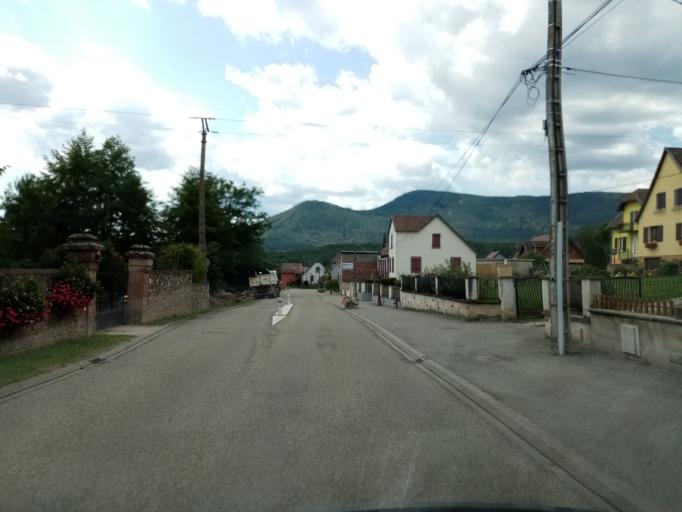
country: FR
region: Alsace
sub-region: Departement du Bas-Rhin
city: Ville
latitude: 48.3228
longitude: 7.3520
